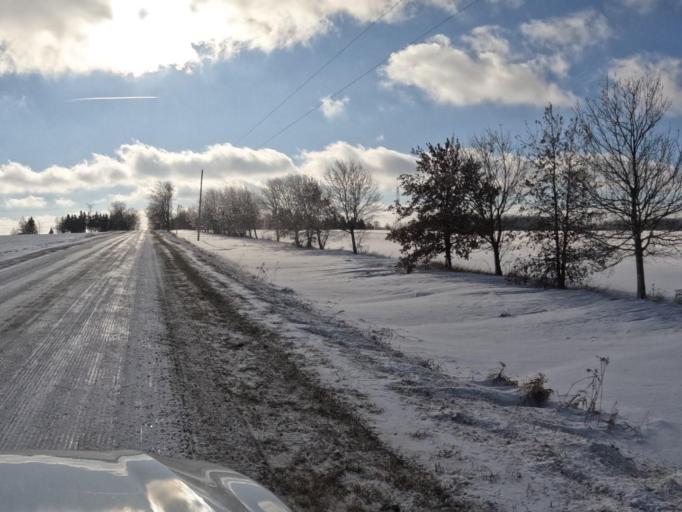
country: CA
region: Ontario
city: Shelburne
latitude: 43.9999
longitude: -80.4095
